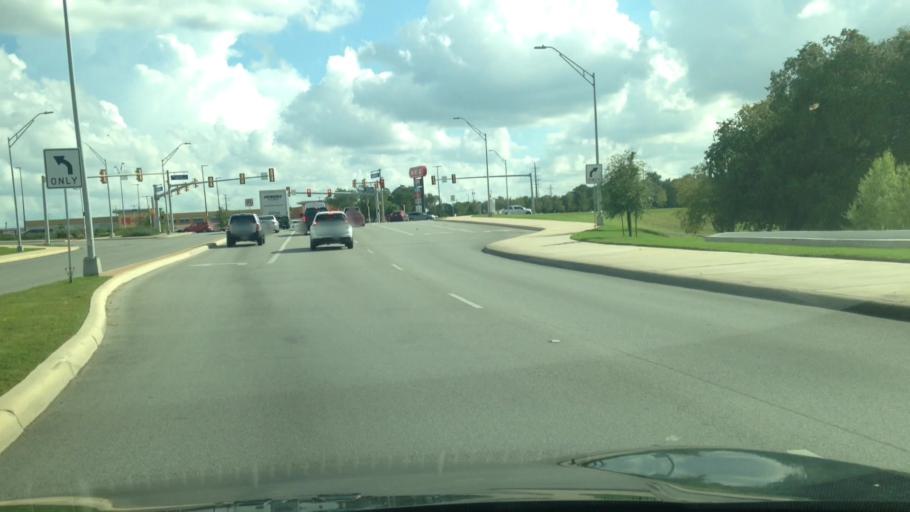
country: US
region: Texas
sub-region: Bexar County
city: Hollywood Park
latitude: 29.5984
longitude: -98.4182
